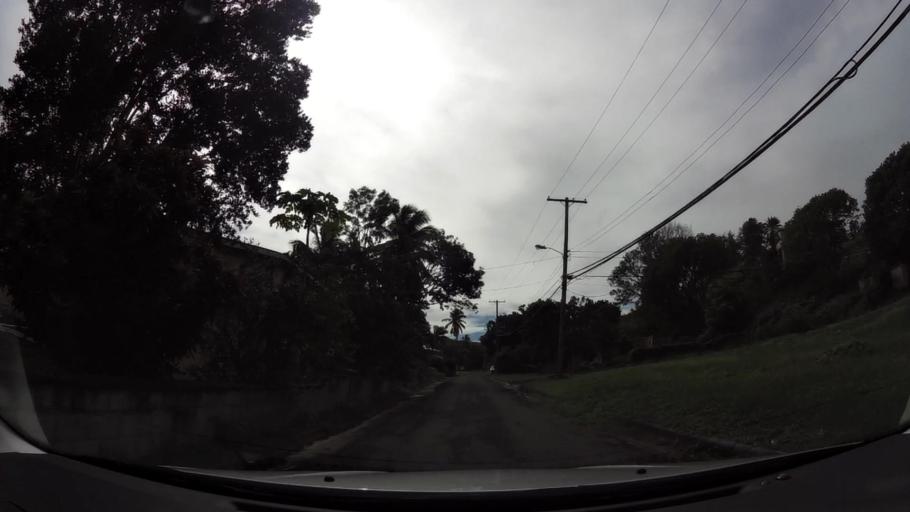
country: AG
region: Saint Peter
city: Parham
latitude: 17.0592
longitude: -61.7241
